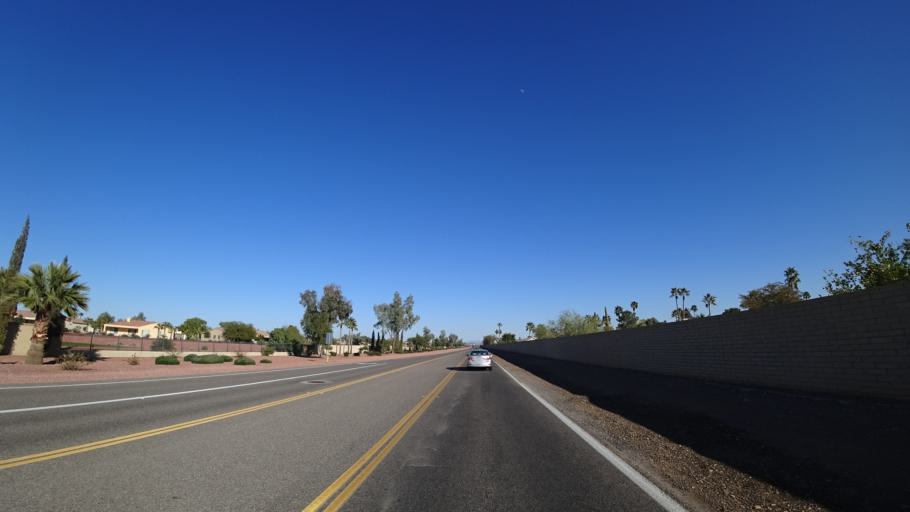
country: US
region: Arizona
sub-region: Maricopa County
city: Sun City West
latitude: 33.6820
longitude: -112.3419
